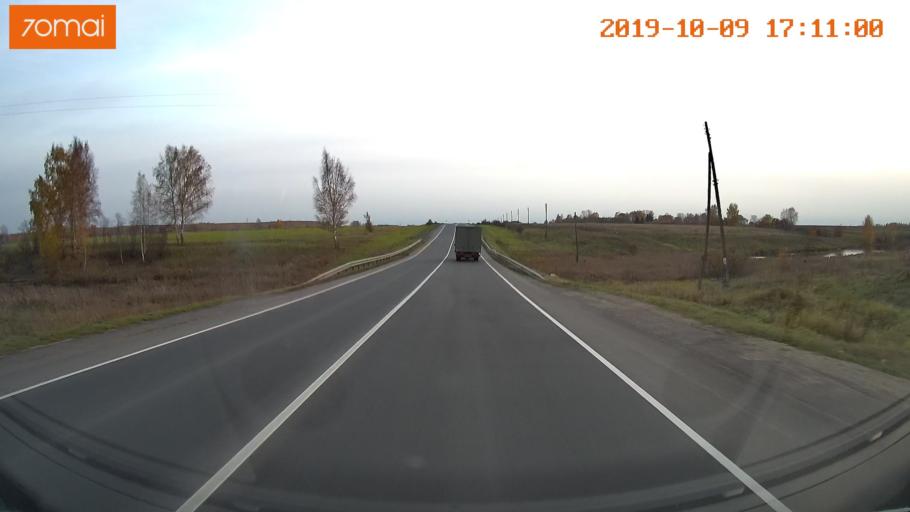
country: RU
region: Ivanovo
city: Privolzhsk
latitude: 57.3483
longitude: 41.2531
